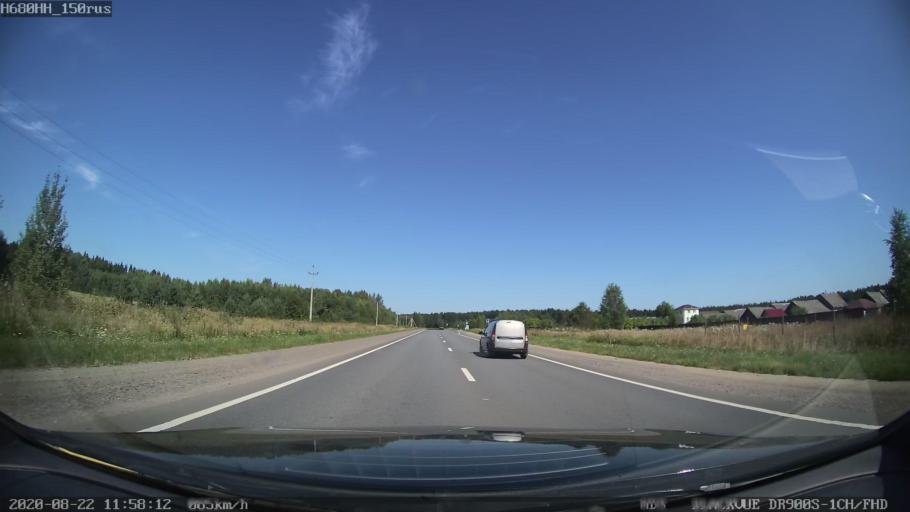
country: RU
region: Tverskaya
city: Rameshki
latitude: 57.1889
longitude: 36.0832
